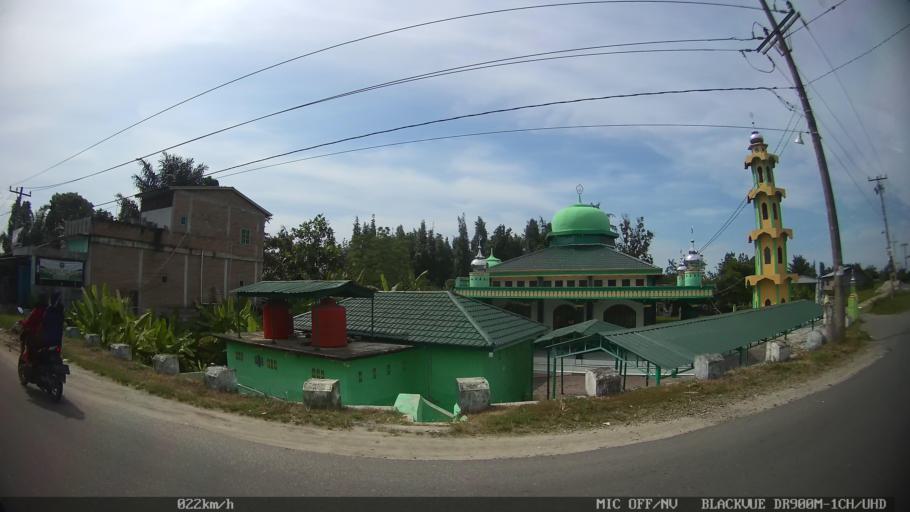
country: ID
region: North Sumatra
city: Percut
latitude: 3.6150
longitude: 98.8327
